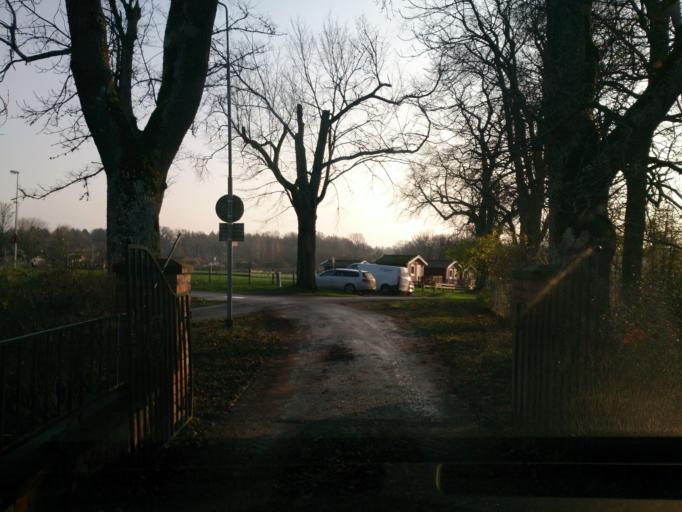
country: SE
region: OEstergoetland
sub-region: Atvidabergs Kommun
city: Atvidaberg
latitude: 58.1923
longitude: 15.9953
